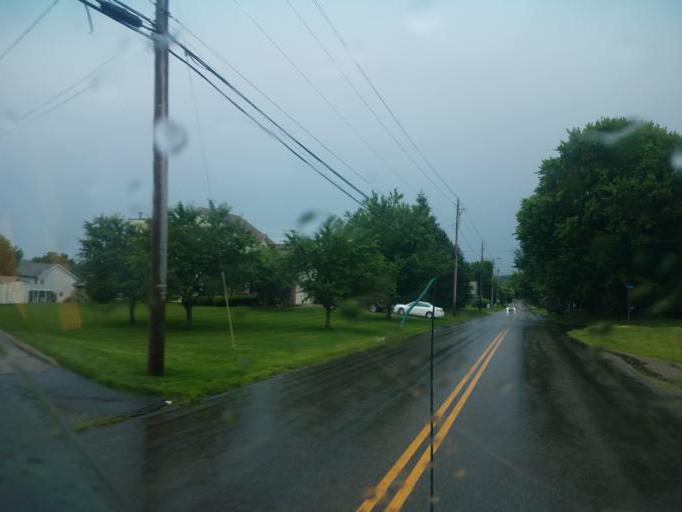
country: US
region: Ohio
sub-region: Stark County
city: Massillon
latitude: 40.7860
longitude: -81.5544
